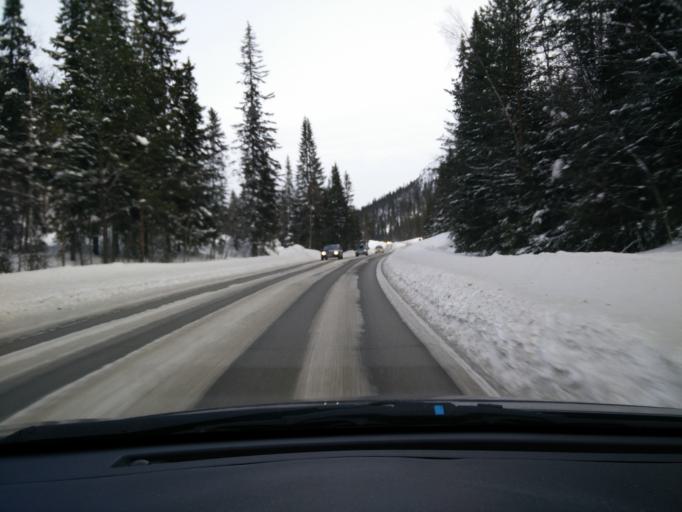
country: SE
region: Jaemtland
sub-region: Bergs Kommun
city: Hoverberg
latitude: 62.4942
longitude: 13.9376
